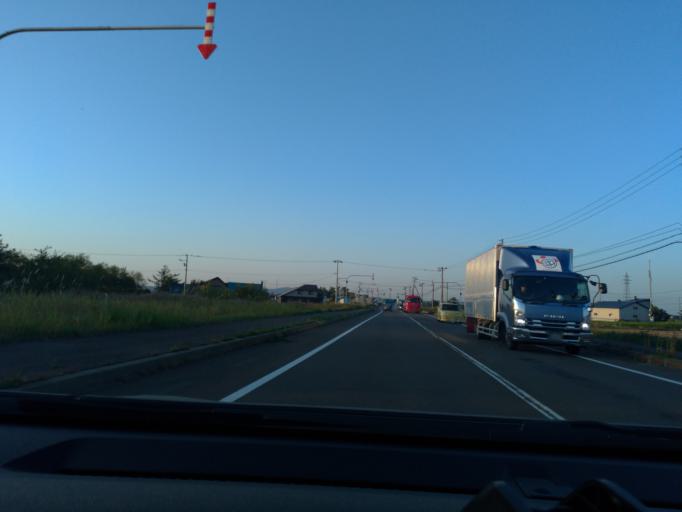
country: JP
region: Hokkaido
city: Tobetsu
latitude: 43.1881
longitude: 141.5243
